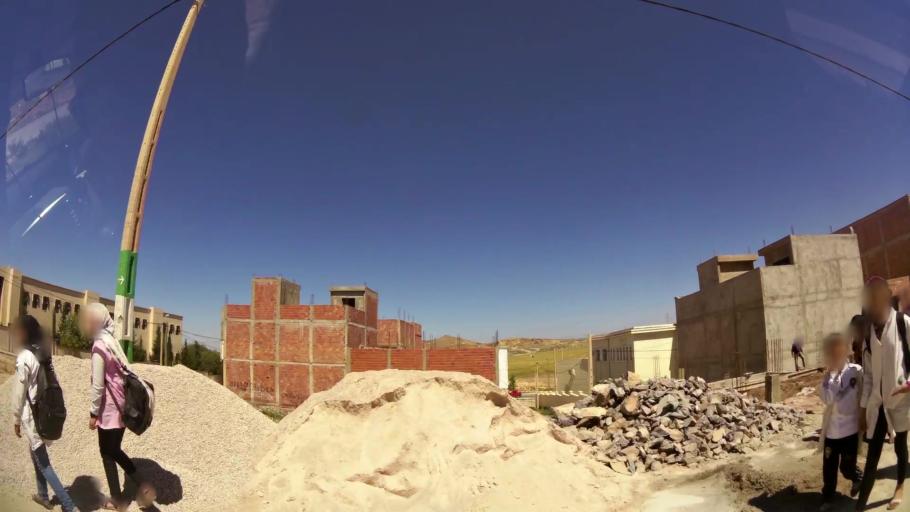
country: MA
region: Oriental
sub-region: Oujda-Angad
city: Oujda
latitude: 34.6573
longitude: -1.8678
